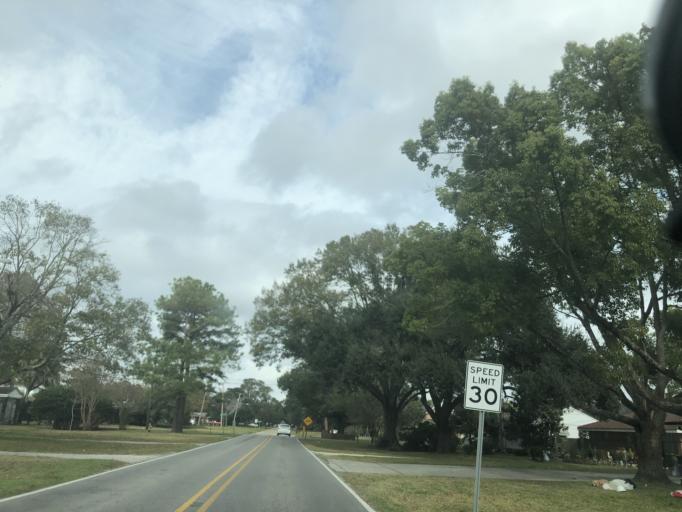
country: US
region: Louisiana
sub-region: Jefferson Parish
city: Metairie Terrace
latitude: 29.9838
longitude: -90.1602
